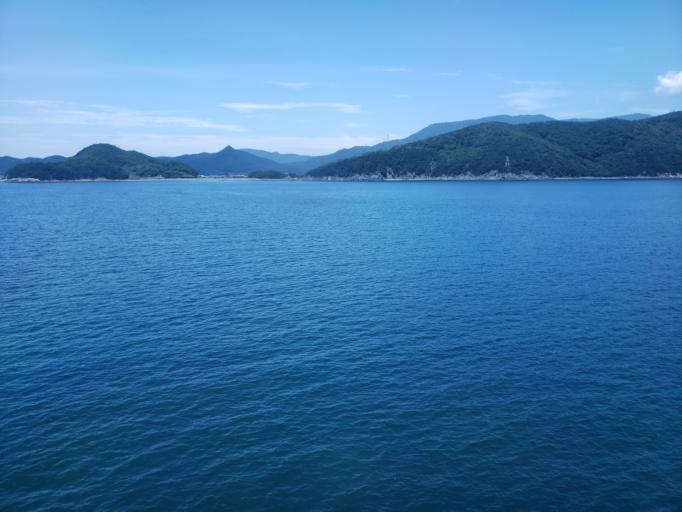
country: JP
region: Kagawa
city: Tonosho
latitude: 34.4380
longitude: 134.2962
